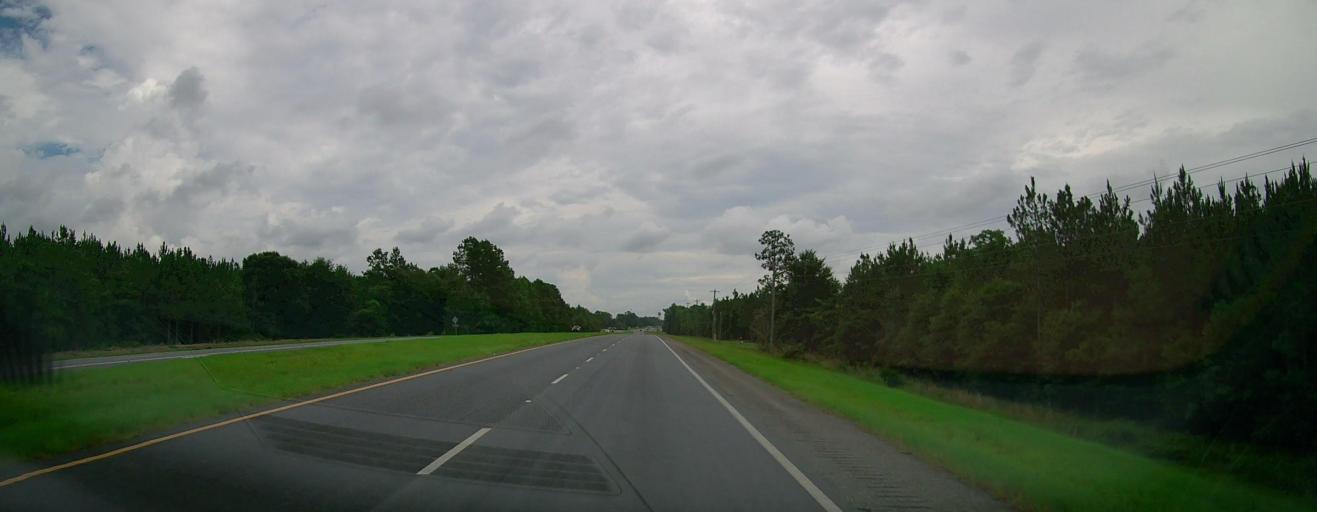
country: US
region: Georgia
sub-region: Dodge County
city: Eastman
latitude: 32.1078
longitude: -83.0846
